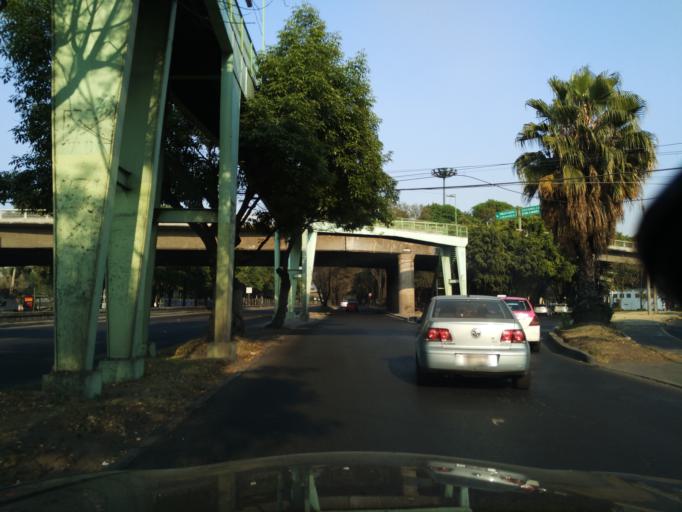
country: MX
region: Mexico City
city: Xochimilco
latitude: 19.2842
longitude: -99.1283
